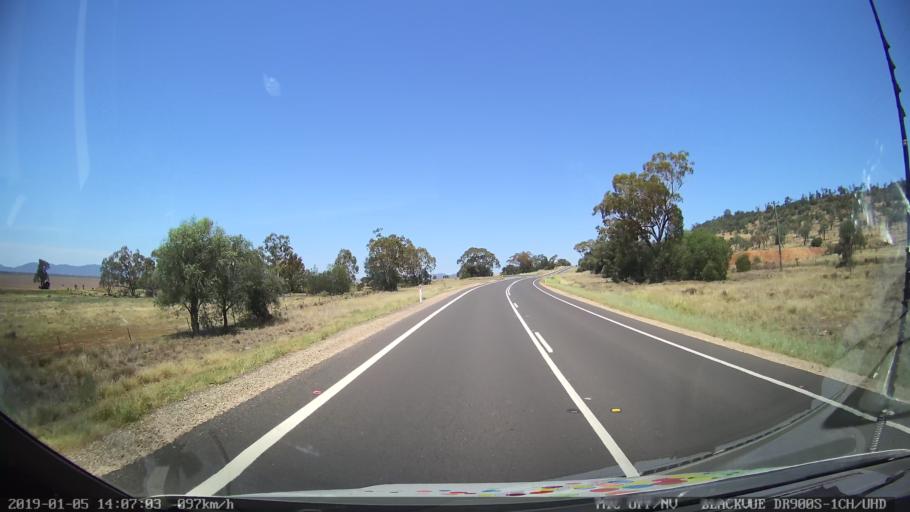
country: AU
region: New South Wales
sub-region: Gunnedah
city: Gunnedah
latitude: -31.2193
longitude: 150.4013
